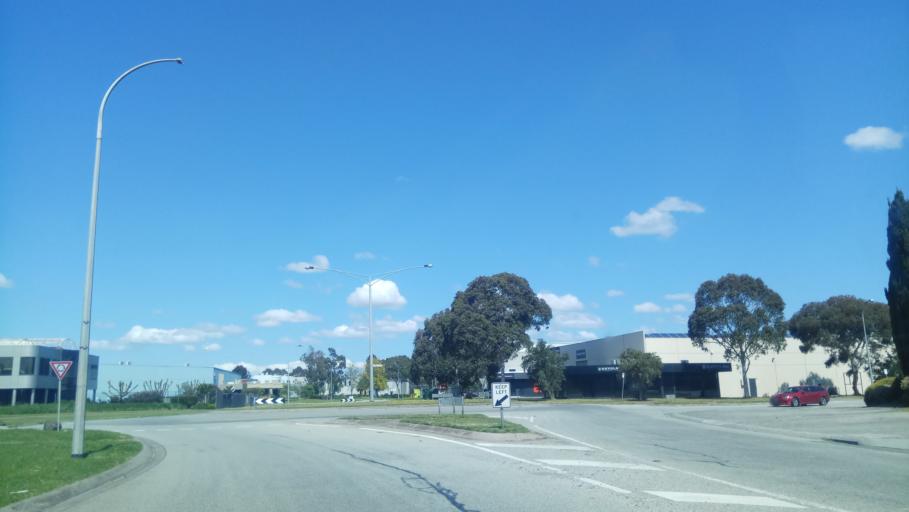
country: AU
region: Victoria
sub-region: Kingston
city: Dingley Village
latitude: -37.9945
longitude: 145.1187
